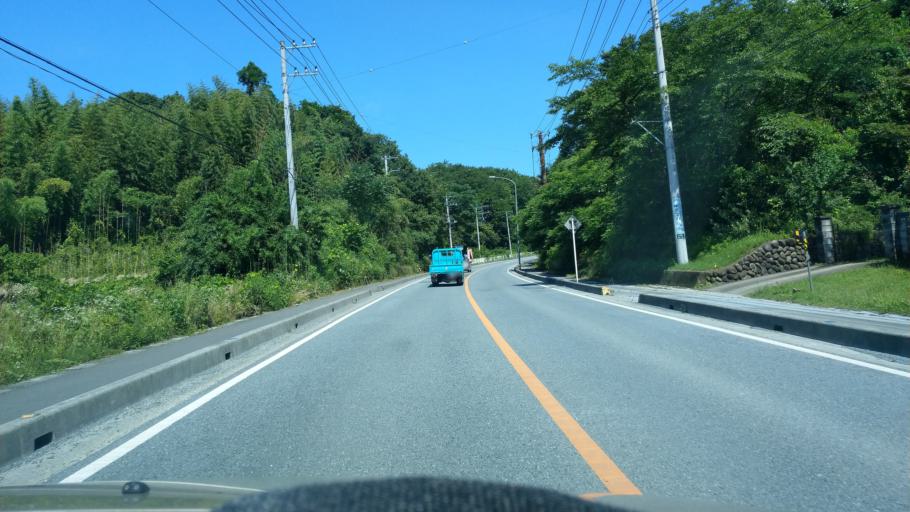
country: JP
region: Saitama
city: Ogawa
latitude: 36.0725
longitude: 139.2481
